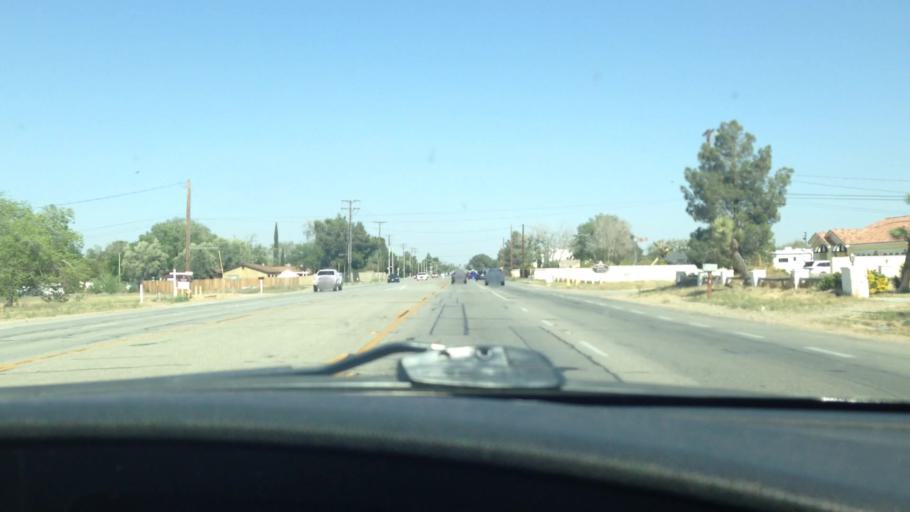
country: US
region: California
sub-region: Los Angeles County
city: Quartz Hill
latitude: 34.6599
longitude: -118.1725
